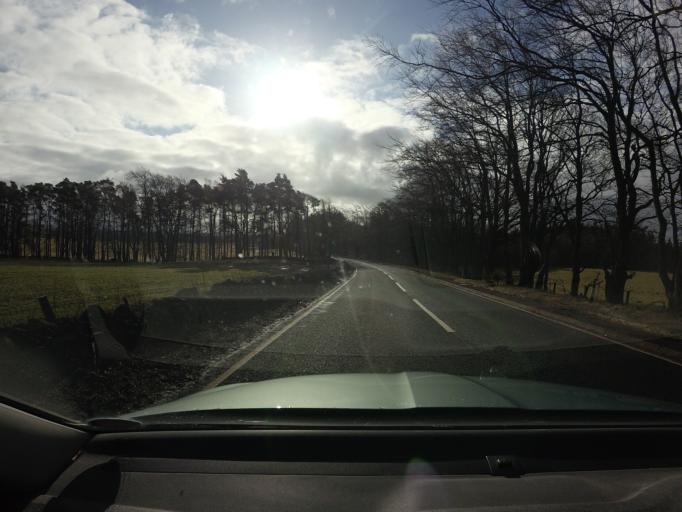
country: GB
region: Scotland
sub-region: South Lanarkshire
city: Forth
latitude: 55.7042
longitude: -3.7203
